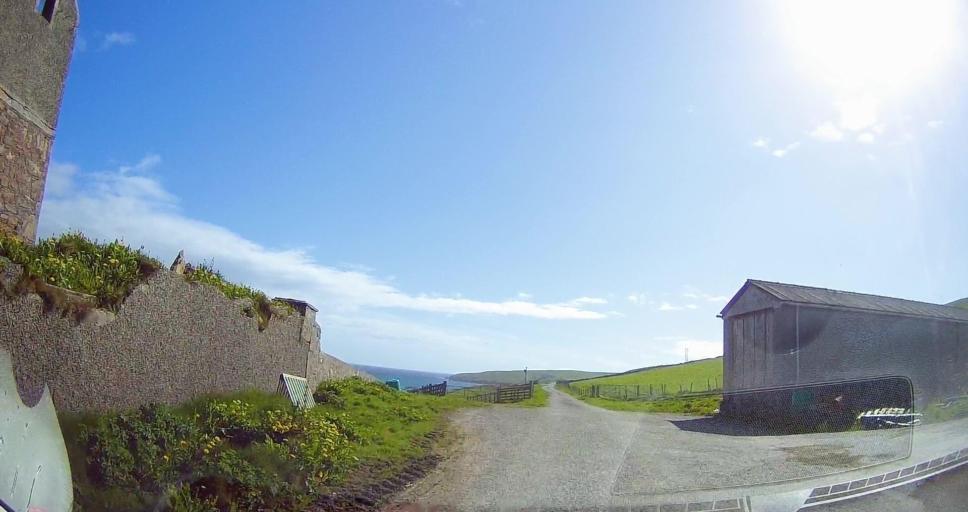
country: GB
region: Scotland
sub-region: Shetland Islands
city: Sandwick
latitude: 59.9018
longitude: -1.3385
